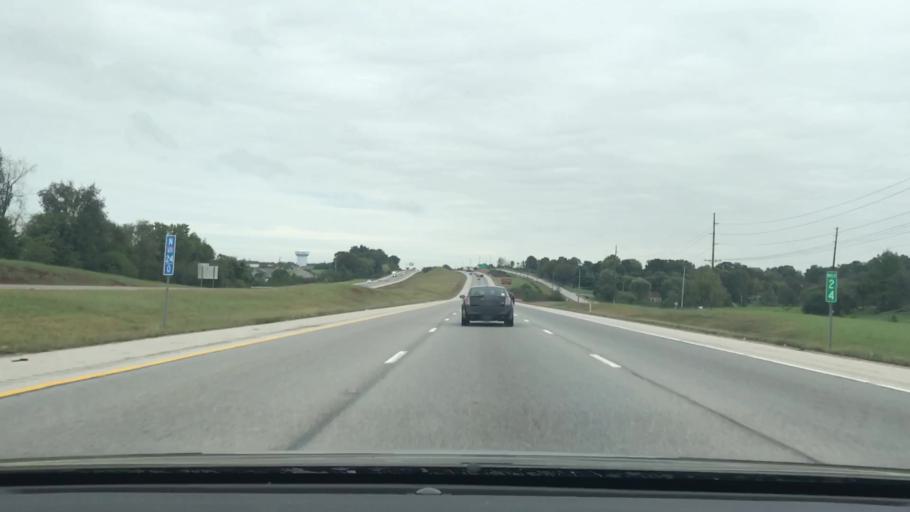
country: US
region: Kentucky
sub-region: Warren County
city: Bowling Green
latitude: 36.9550
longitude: -86.4047
